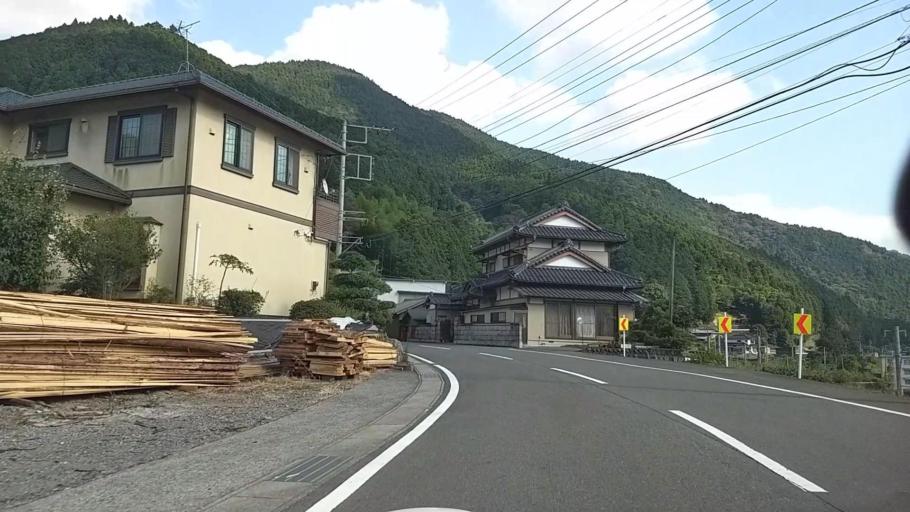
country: JP
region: Shizuoka
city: Fujinomiya
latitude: 35.2794
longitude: 138.4676
